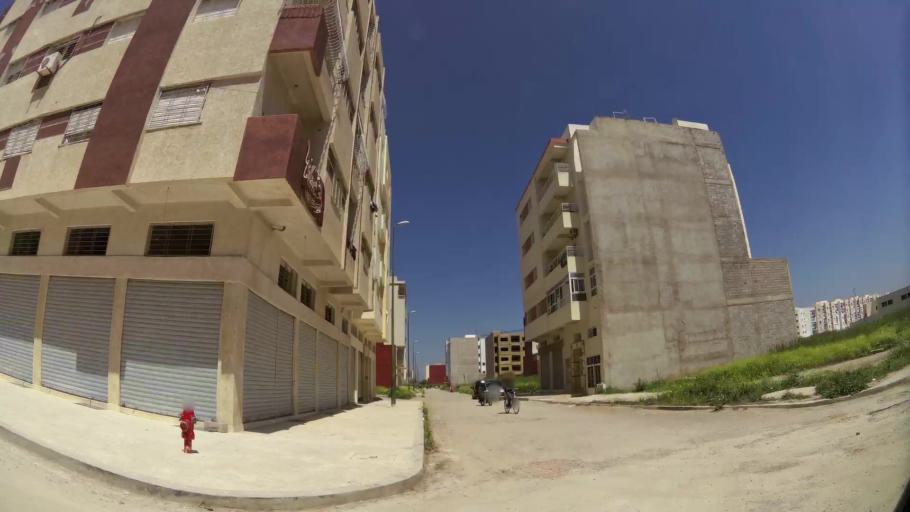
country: MA
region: Fes-Boulemane
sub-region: Fes
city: Fes
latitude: 34.0274
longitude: -5.0449
